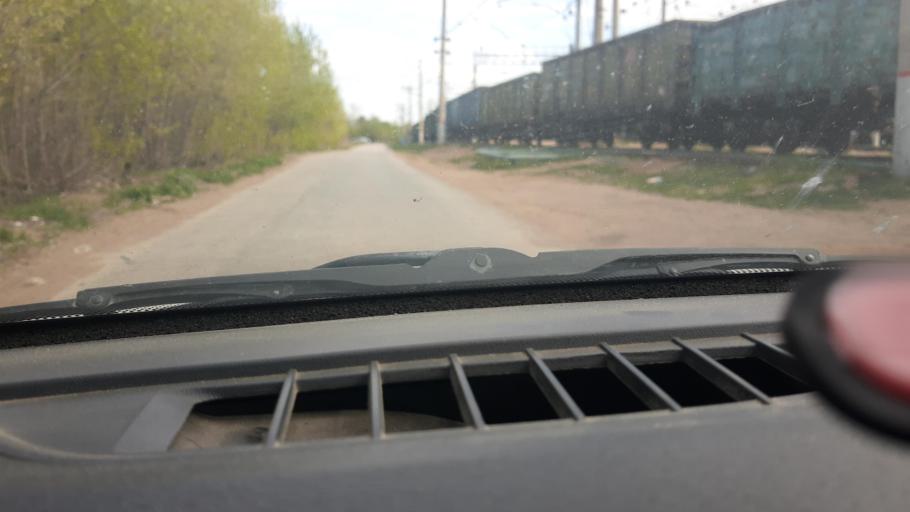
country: RU
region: Bashkortostan
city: Avdon
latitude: 54.6479
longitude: 55.8391
